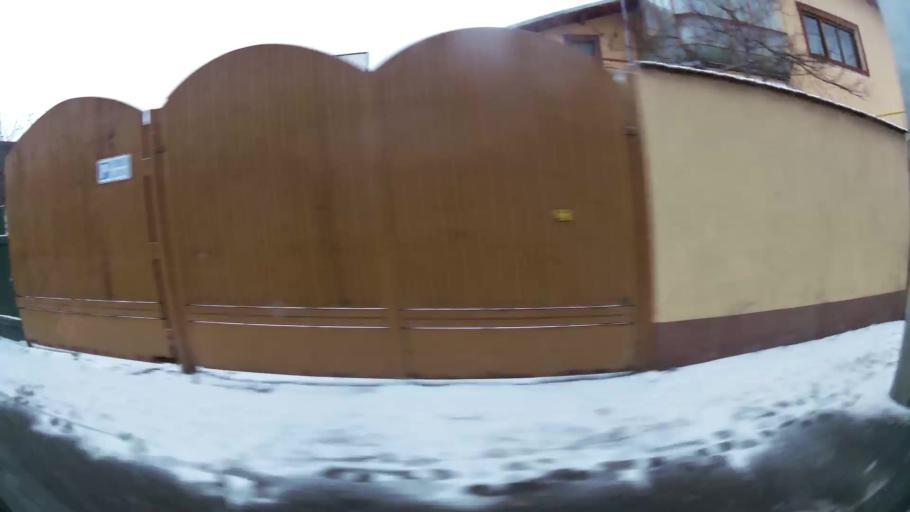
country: RO
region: Prahova
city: Ploiesti
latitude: 44.9352
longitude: 26.0399
